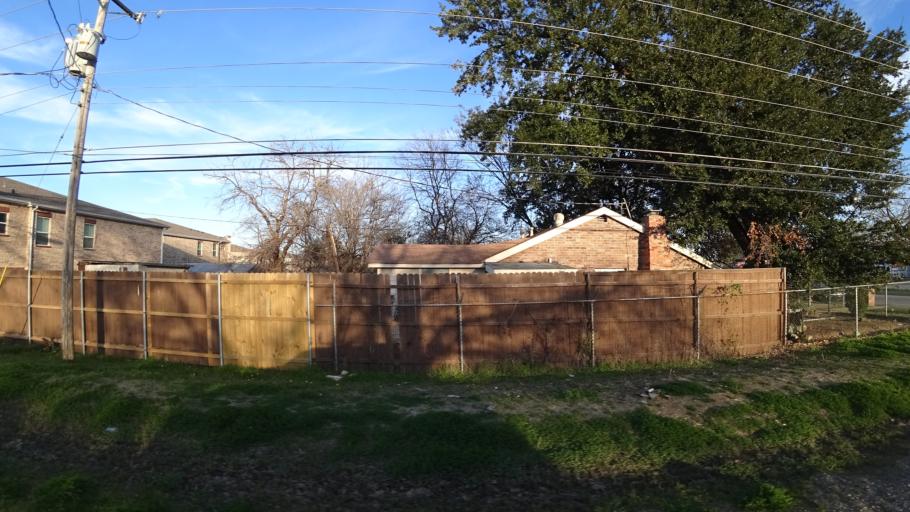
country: US
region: Texas
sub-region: Denton County
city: Lewisville
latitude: 33.0433
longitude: -96.9928
